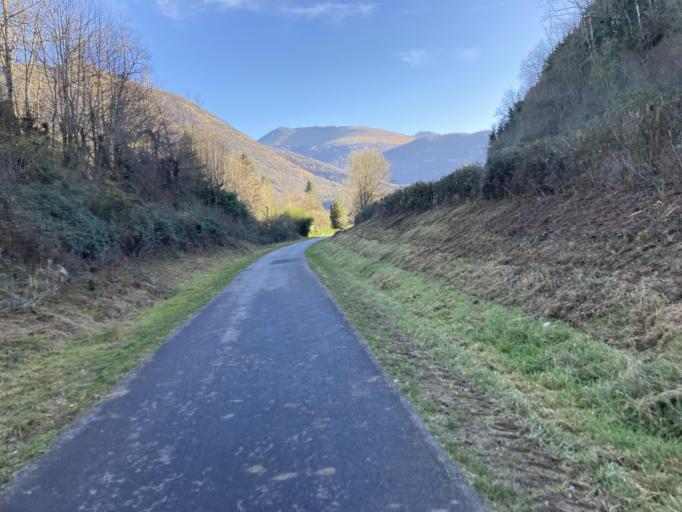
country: FR
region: Aquitaine
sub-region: Departement des Pyrenees-Atlantiques
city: Louvie-Juzon
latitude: 43.0890
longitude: -0.4268
